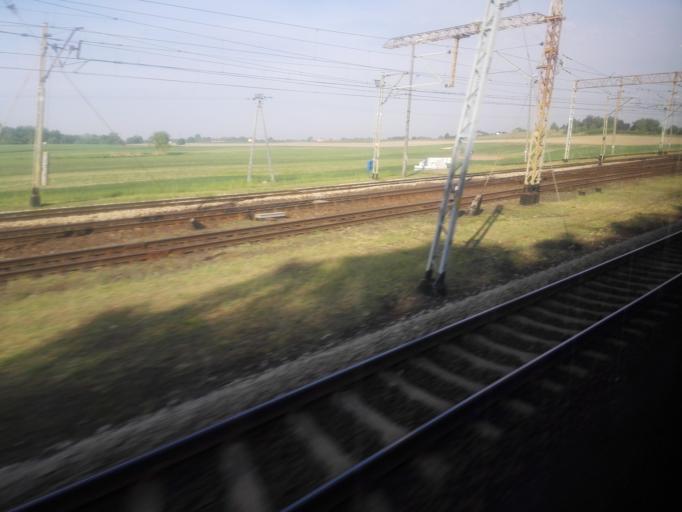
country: PL
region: Greater Poland Voivodeship
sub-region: Powiat wrzesinski
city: Wrzesnia
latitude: 52.3382
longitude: 17.4922
